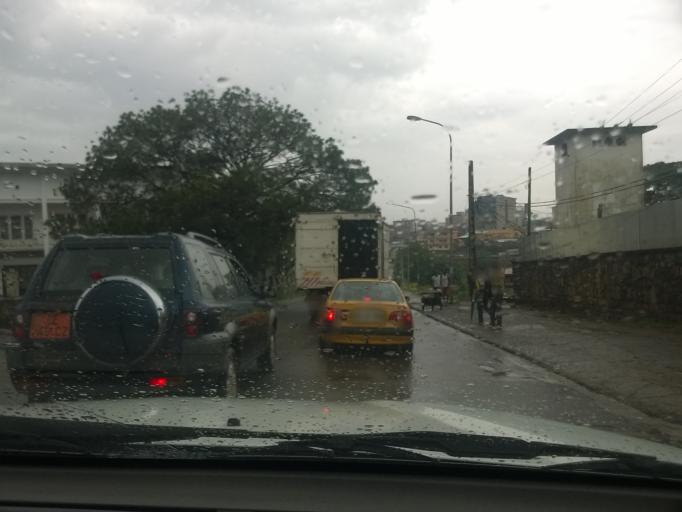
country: CM
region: Centre
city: Yaounde
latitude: 3.8736
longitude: 11.5293
